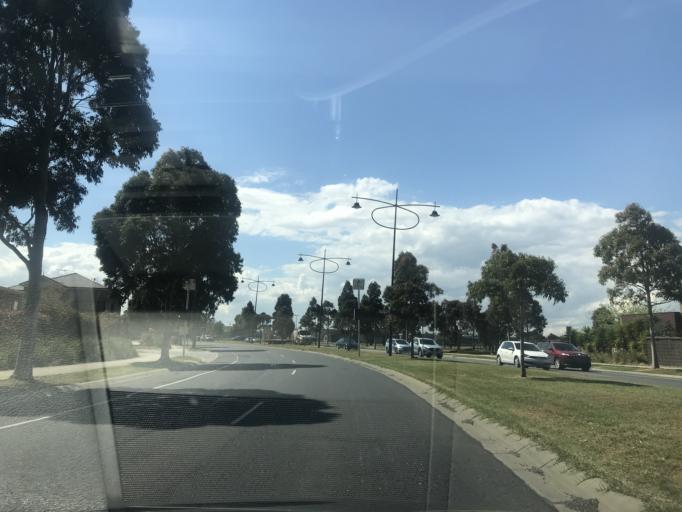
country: AU
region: Victoria
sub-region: Wyndham
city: Williams Landing
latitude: -37.8903
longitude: 144.7323
